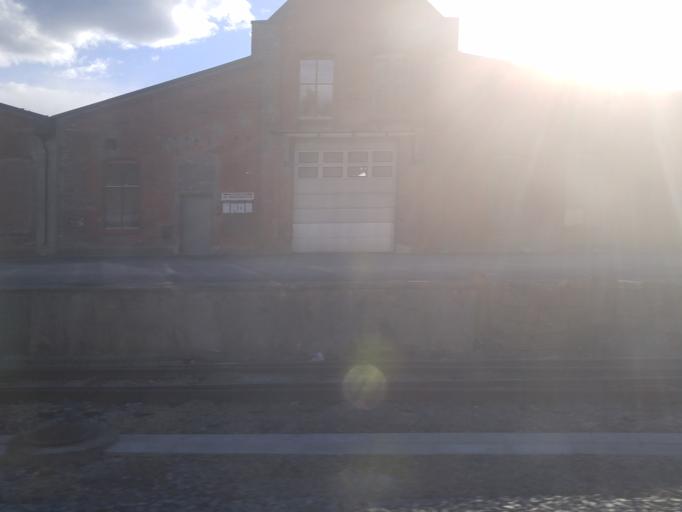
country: NO
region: Hedmark
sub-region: Ringsaker
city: Moelv
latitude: 60.9319
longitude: 10.6951
